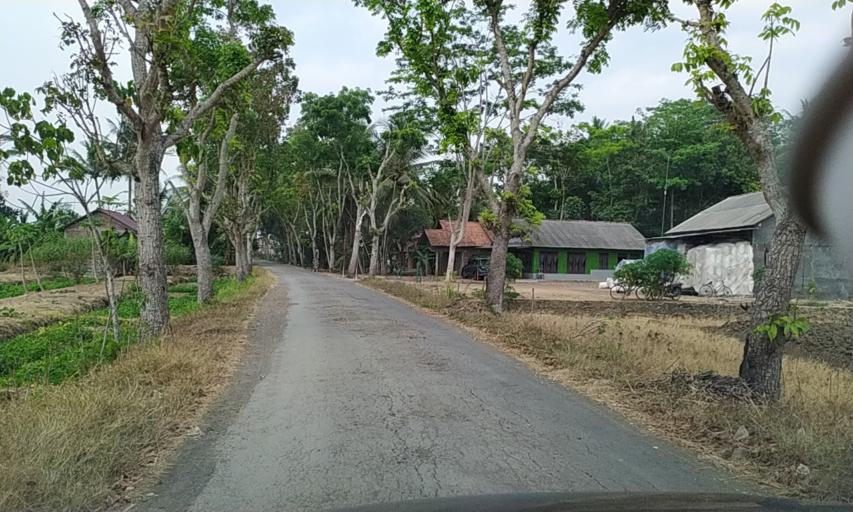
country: ID
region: Central Java
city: Alurbulu
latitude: -7.5234
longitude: 108.8419
